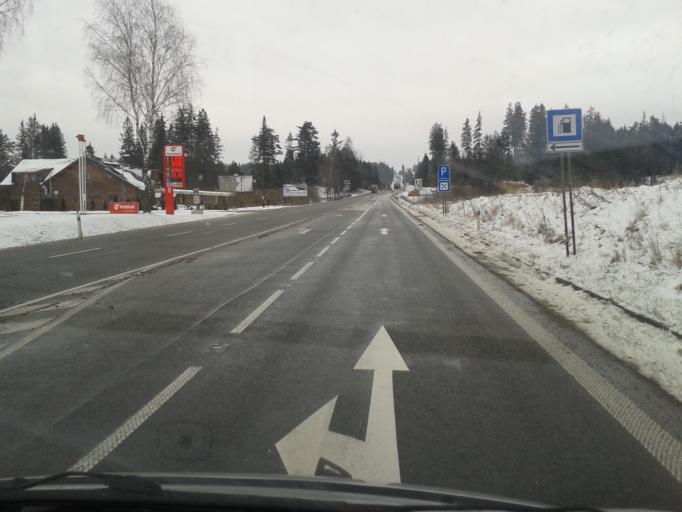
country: PL
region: Lesser Poland Voivodeship
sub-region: Powiat nowotarski
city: Chyzne
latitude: 49.4005
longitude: 19.6509
